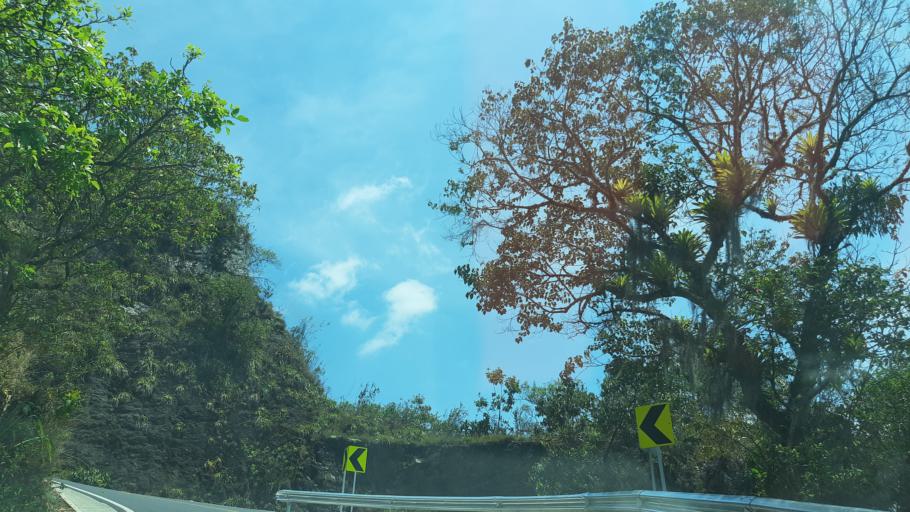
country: CO
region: Boyaca
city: Chinavita
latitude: 5.1311
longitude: -73.3883
